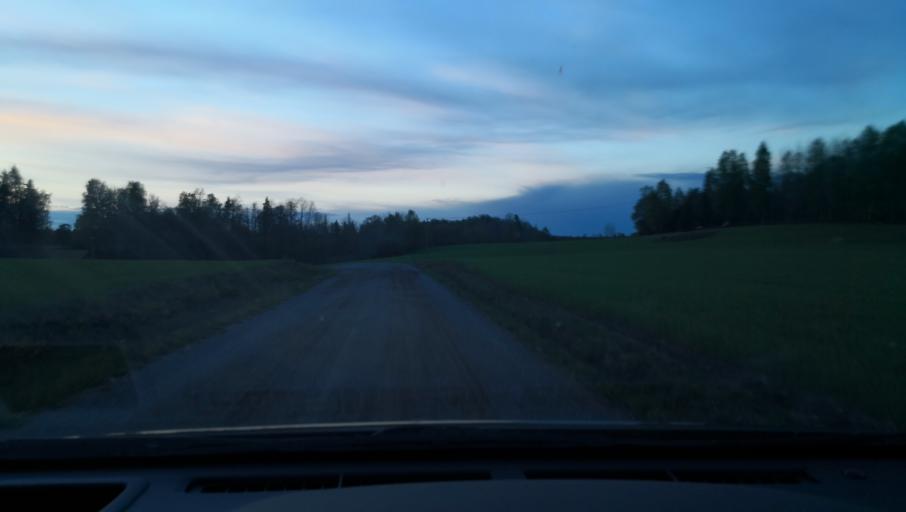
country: SE
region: OErebro
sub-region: Askersunds Kommun
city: Askersund
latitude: 58.9914
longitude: 14.9066
